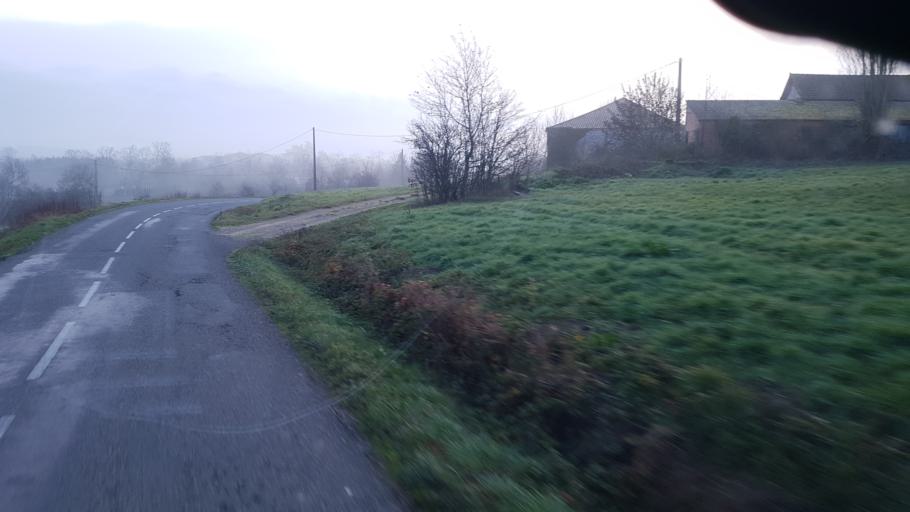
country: FR
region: Midi-Pyrenees
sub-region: Departement du Tarn-et-Garonne
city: Caussade
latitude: 44.2104
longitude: 1.5216
